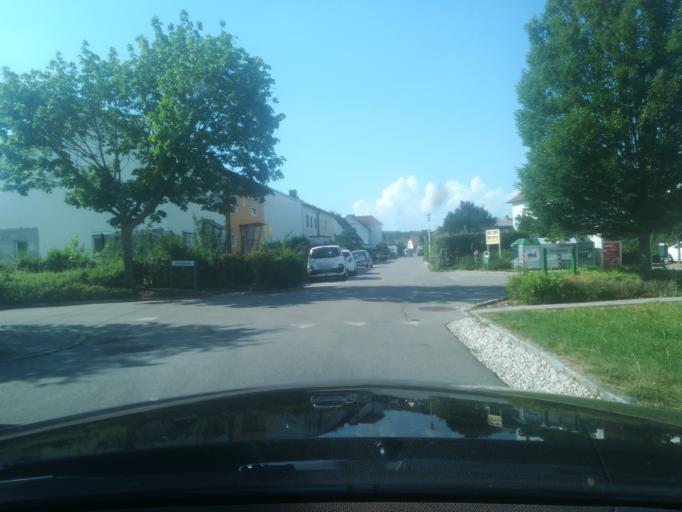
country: AT
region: Upper Austria
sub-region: Politischer Bezirk Linz-Land
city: Traun
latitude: 48.2408
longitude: 14.2452
